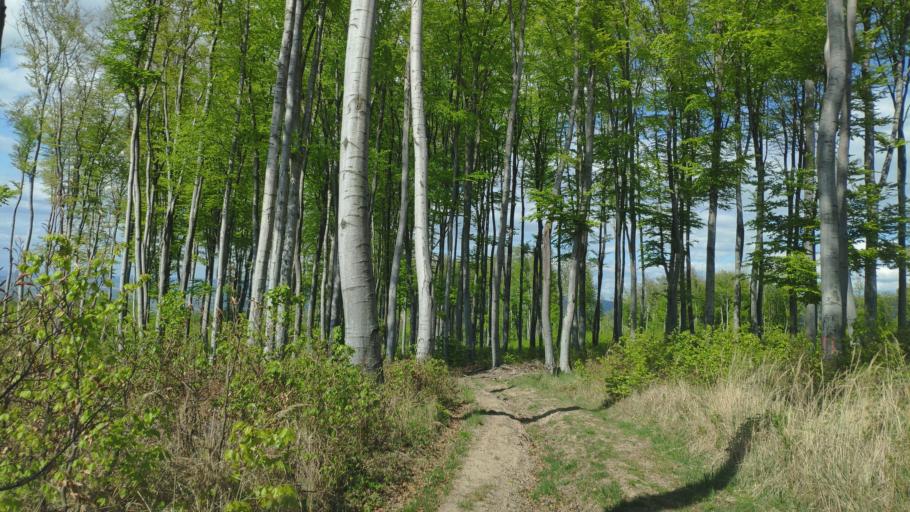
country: SK
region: Kosicky
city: Kosice
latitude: 48.6613
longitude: 21.4485
